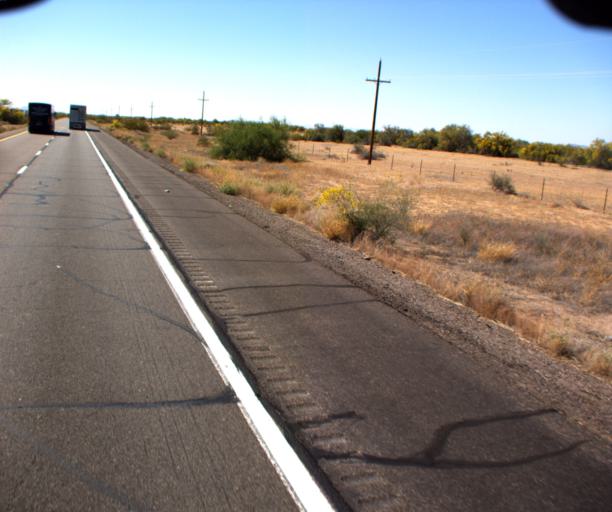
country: US
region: Arizona
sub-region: Maricopa County
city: Gila Bend
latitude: 32.8447
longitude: -113.2889
